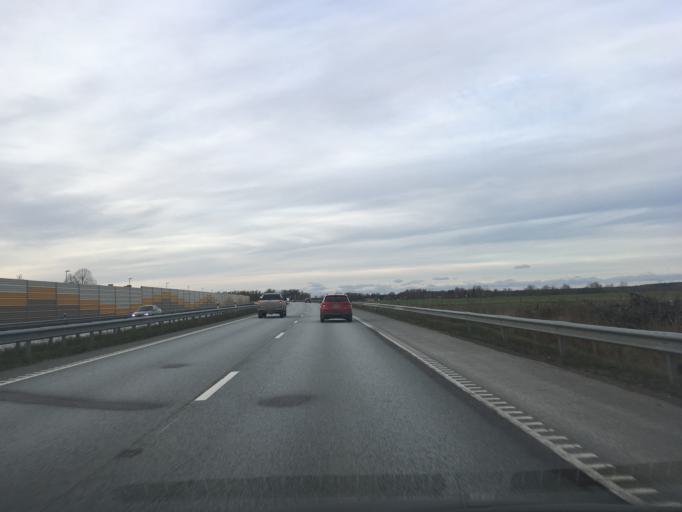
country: EE
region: Ida-Virumaa
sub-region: Johvi vald
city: Johvi
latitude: 59.3781
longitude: 27.3749
